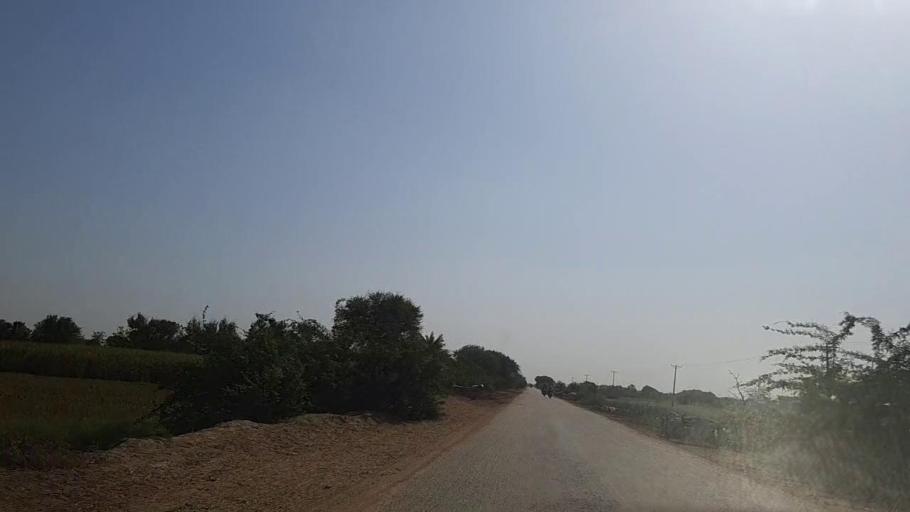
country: PK
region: Sindh
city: Mirpur Batoro
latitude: 24.5965
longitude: 68.2934
